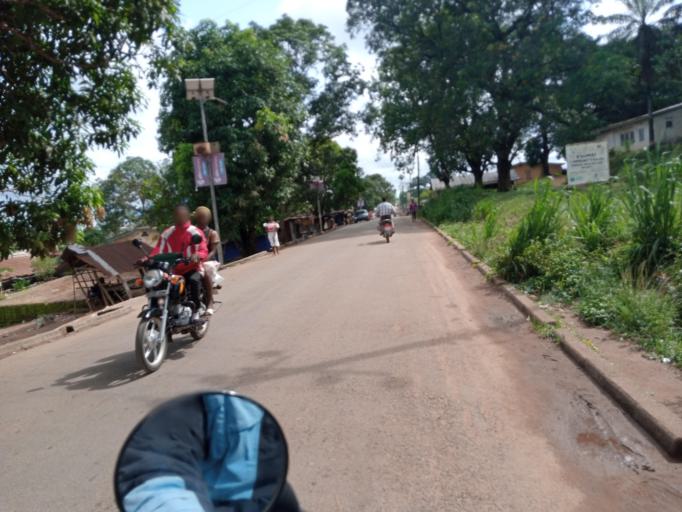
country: SL
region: Southern Province
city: Bo
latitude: 7.9766
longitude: -11.7392
